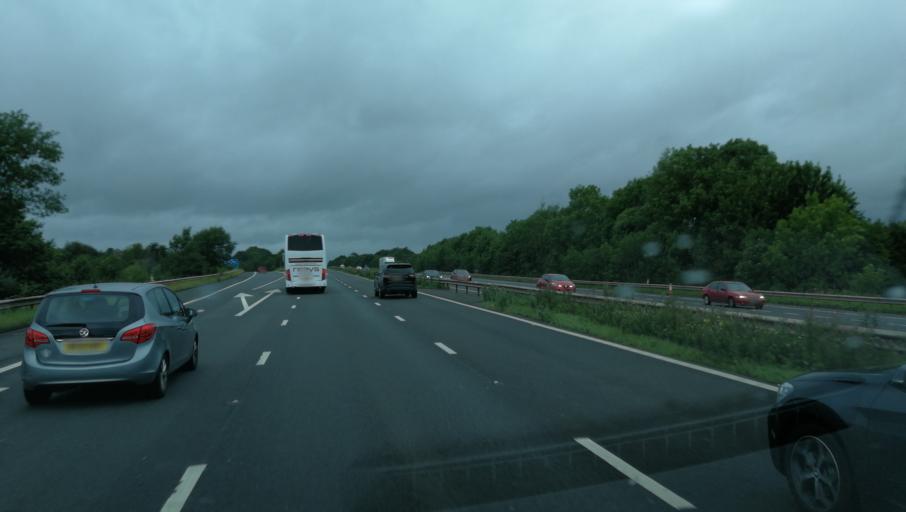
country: GB
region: England
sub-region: Borough of Wigan
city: Atherton
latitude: 53.5533
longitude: -2.4837
